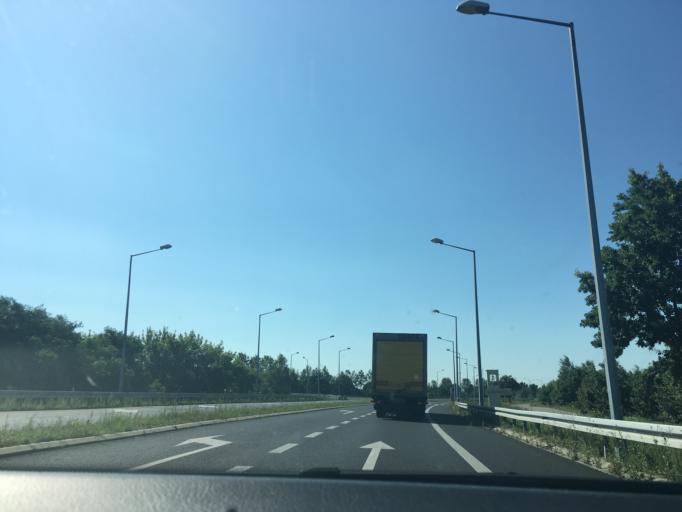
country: PL
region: Lublin Voivodeship
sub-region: Powiat lubartowski
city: Lubartow
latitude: 51.4809
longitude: 22.5888
